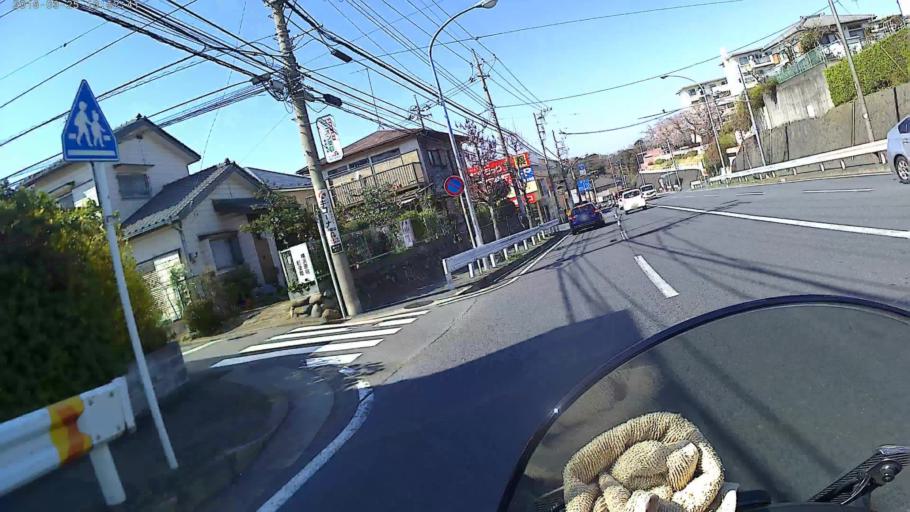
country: JP
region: Kanagawa
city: Fujisawa
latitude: 35.3806
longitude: 139.5028
